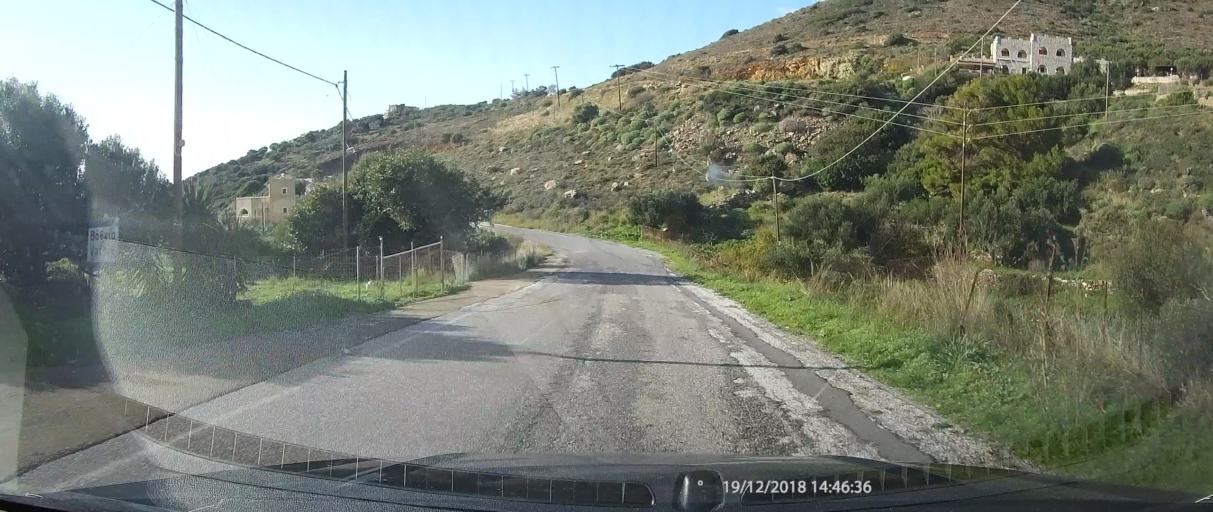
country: GR
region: Peloponnese
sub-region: Nomos Lakonias
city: Gytheio
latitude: 36.4563
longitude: 22.4534
